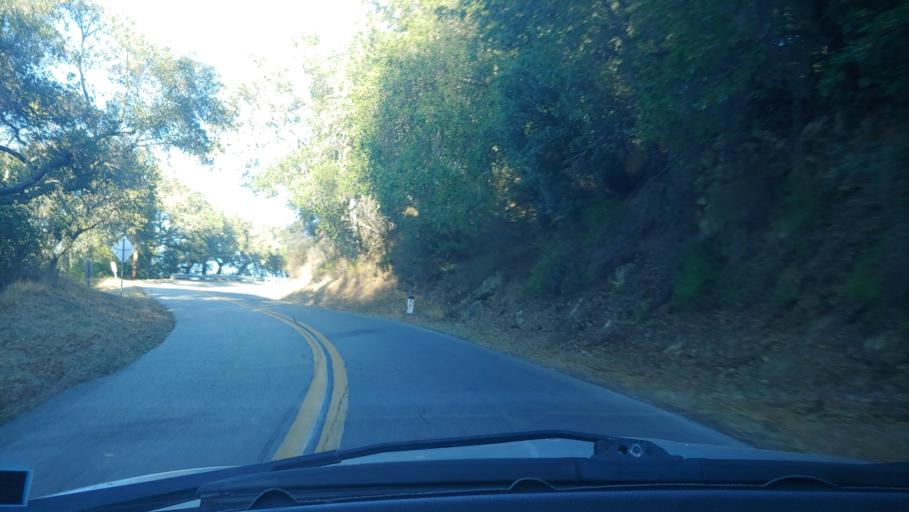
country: US
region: California
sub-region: Santa Barbara County
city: Goleta
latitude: 34.5236
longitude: -119.8342
